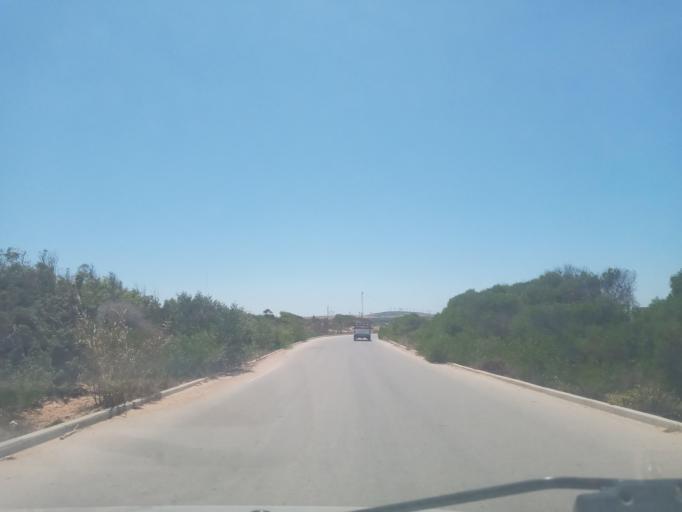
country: TN
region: Nabul
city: El Haouaria
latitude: 37.0508
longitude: 10.9831
